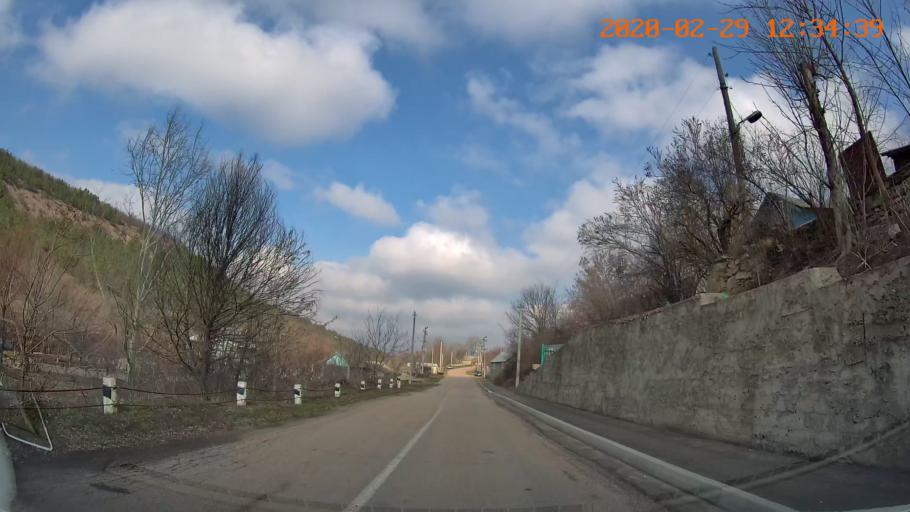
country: MD
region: Telenesti
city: Camenca
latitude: 48.0410
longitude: 28.7155
